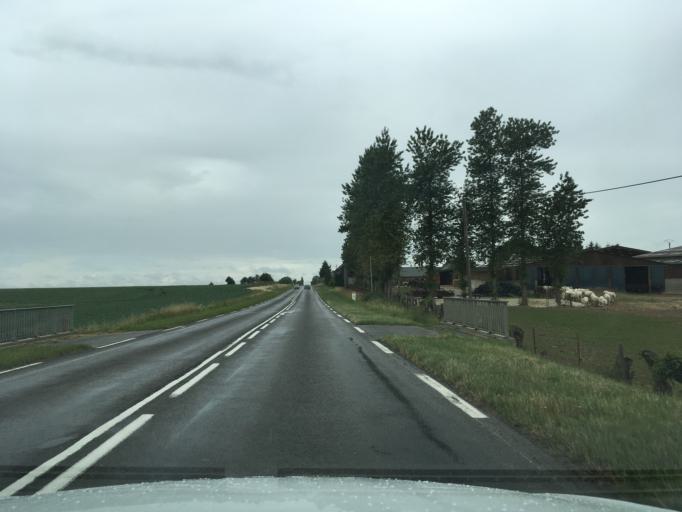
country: FR
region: Picardie
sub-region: Departement de l'Aisne
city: Esqueheries
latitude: 49.9363
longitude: 3.7320
